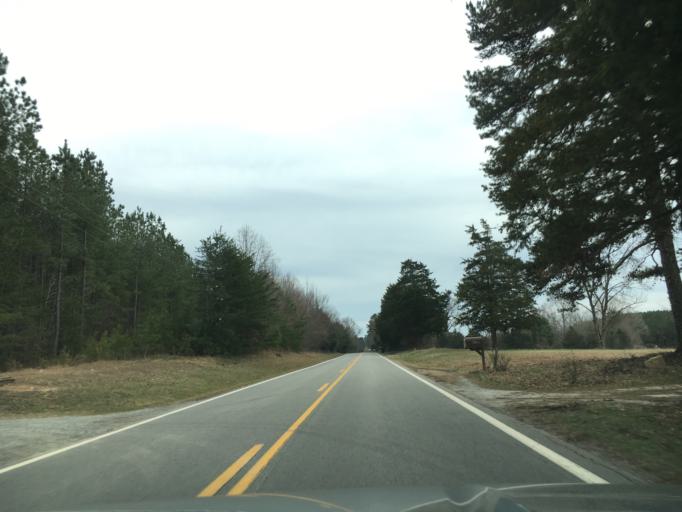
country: US
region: Virginia
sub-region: Charlotte County
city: Charlotte Court House
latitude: 37.0088
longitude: -78.6979
